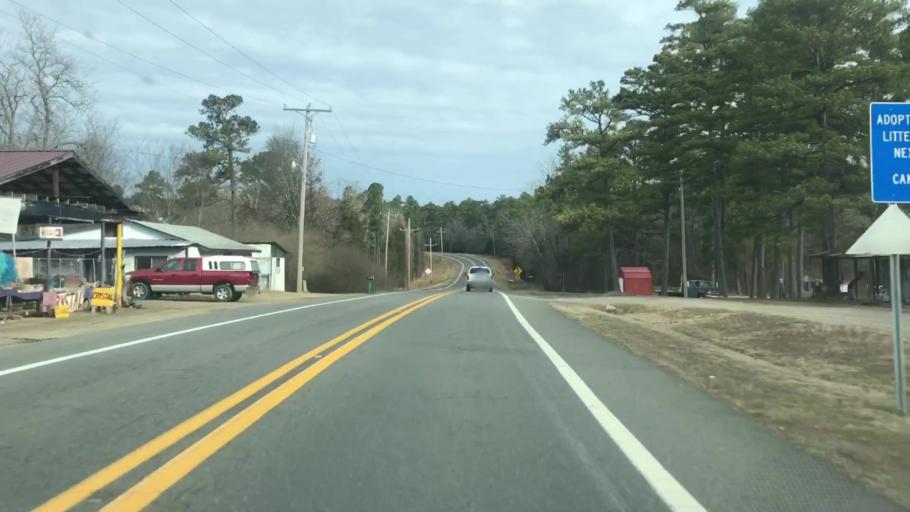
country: US
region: Arkansas
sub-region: Montgomery County
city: Mount Ida
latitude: 34.5851
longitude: -93.6633
